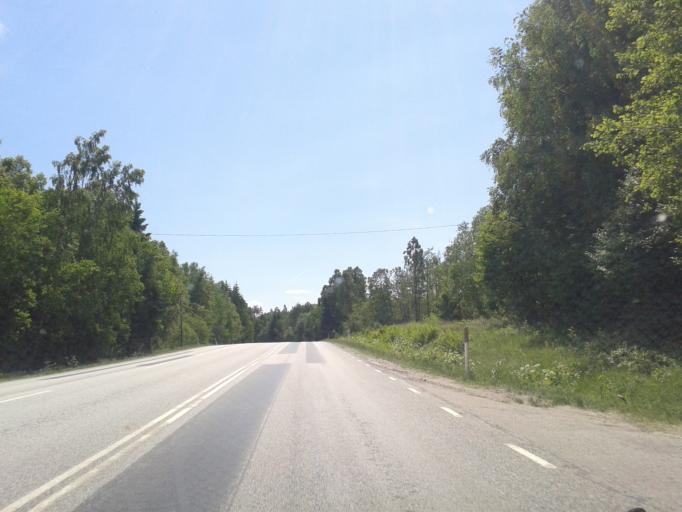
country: SE
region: Vaestra Goetaland
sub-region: Uddevalla Kommun
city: Ljungskile
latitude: 58.1190
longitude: 11.9853
